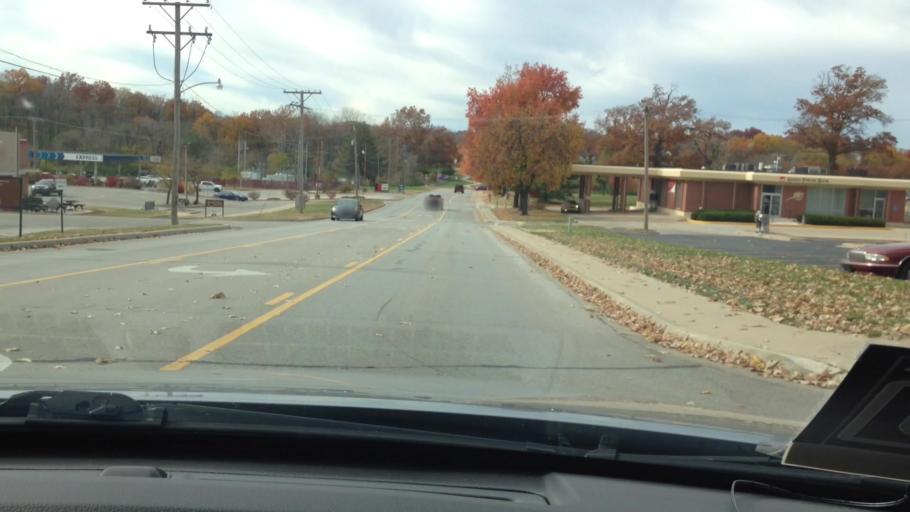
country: US
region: Kansas
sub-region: Leavenworth County
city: Leavenworth
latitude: 39.3383
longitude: -94.9222
